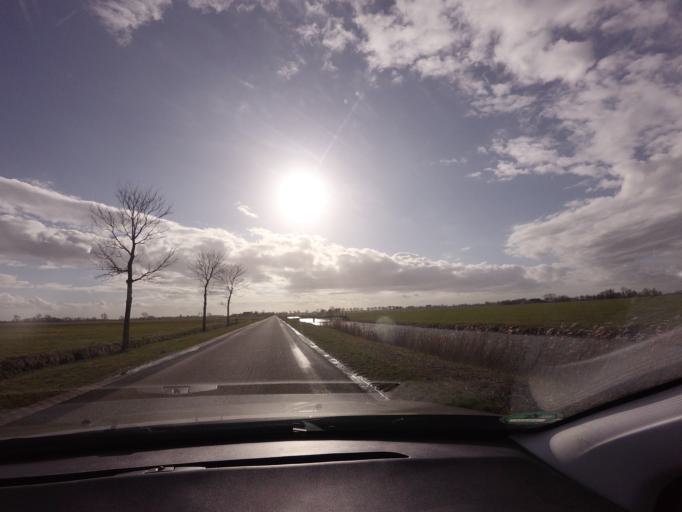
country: NL
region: Friesland
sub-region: Sudwest Fryslan
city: Oppenhuizen
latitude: 53.0459
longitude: 5.7196
